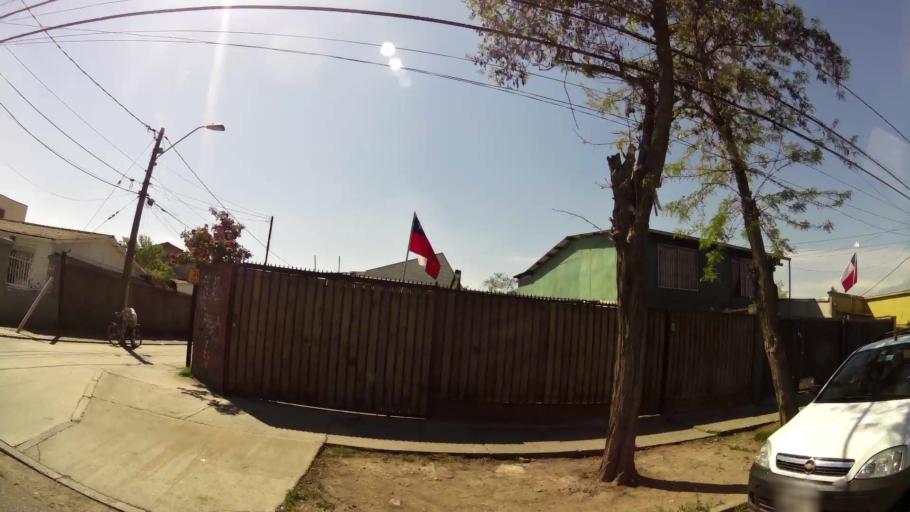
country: CL
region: Santiago Metropolitan
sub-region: Provincia de Santiago
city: Santiago
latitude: -33.5078
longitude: -70.6402
